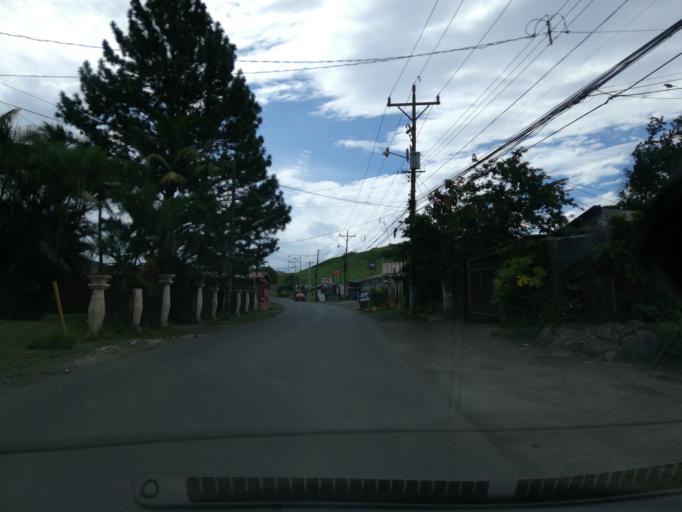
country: CR
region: Alajuela
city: Alajuela
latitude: 9.9957
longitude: -84.2176
